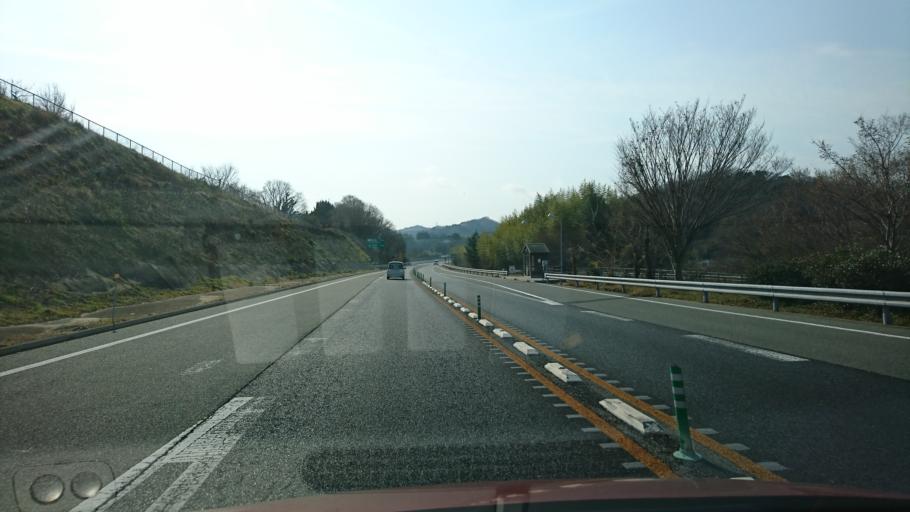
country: JP
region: Hiroshima
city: Onomichi
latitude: 34.3979
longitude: 133.2086
